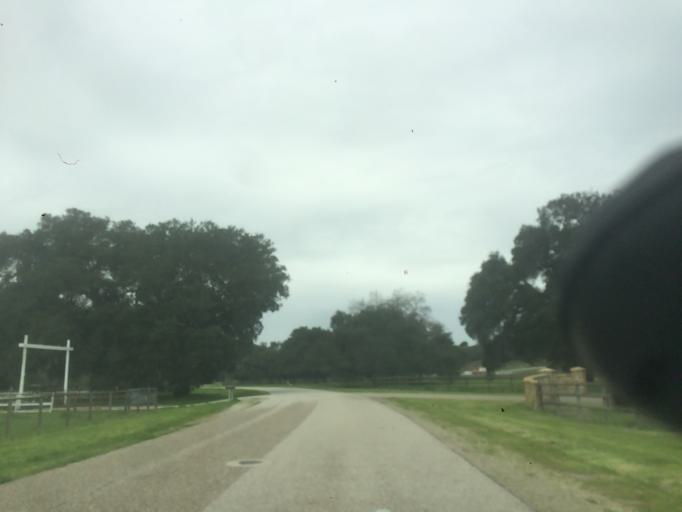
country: US
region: California
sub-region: San Luis Obispo County
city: Nipomo
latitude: 35.2074
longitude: -120.3868
